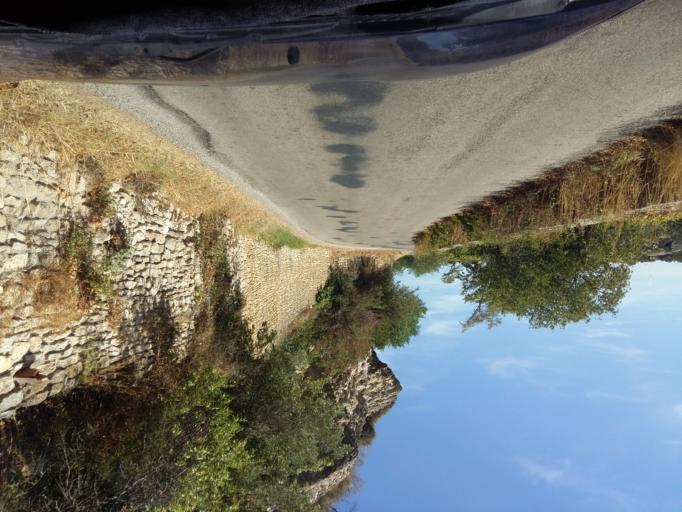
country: FR
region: Provence-Alpes-Cote d'Azur
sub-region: Departement du Vaucluse
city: Venasque
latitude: 43.9970
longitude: 5.1441
